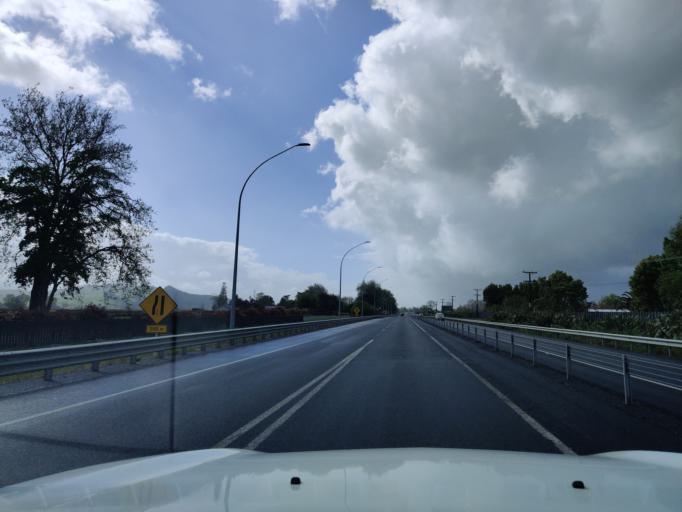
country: NZ
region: Waikato
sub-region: Waipa District
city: Cambridge
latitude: -37.8978
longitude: 175.5098
